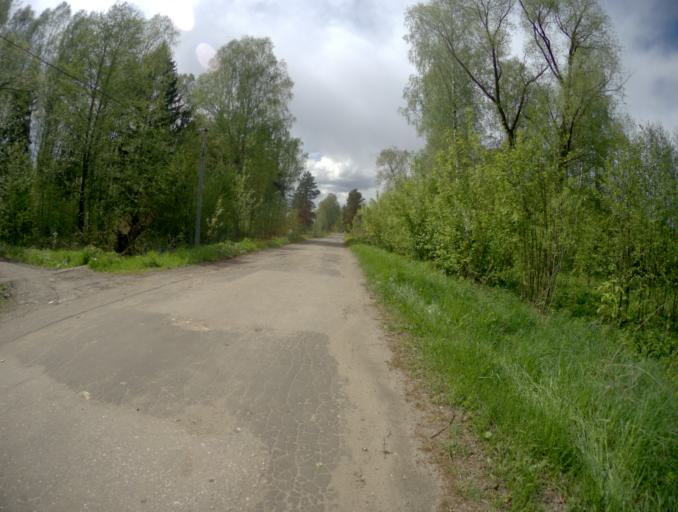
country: RU
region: Vladimir
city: Velikodvorskiy
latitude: 55.2409
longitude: 40.6657
